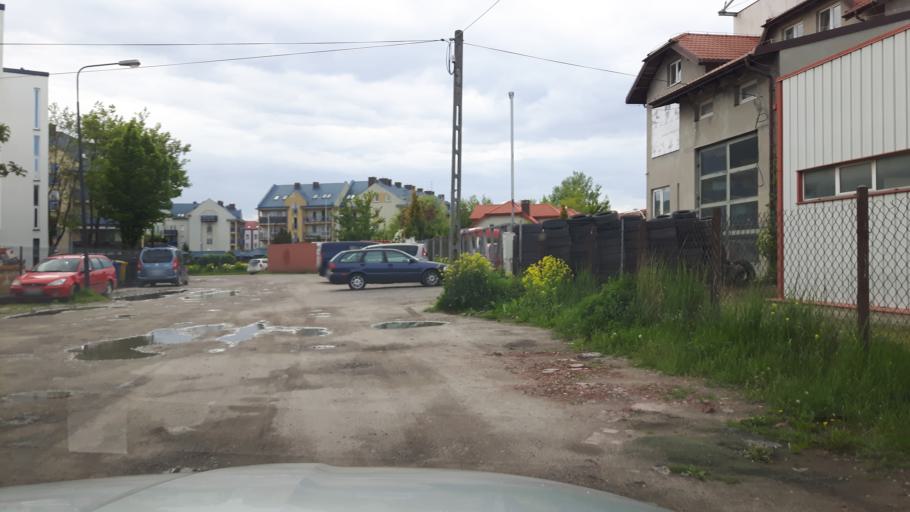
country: PL
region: Masovian Voivodeship
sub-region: Powiat wolominski
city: Zabki
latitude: 52.2888
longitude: 21.0865
